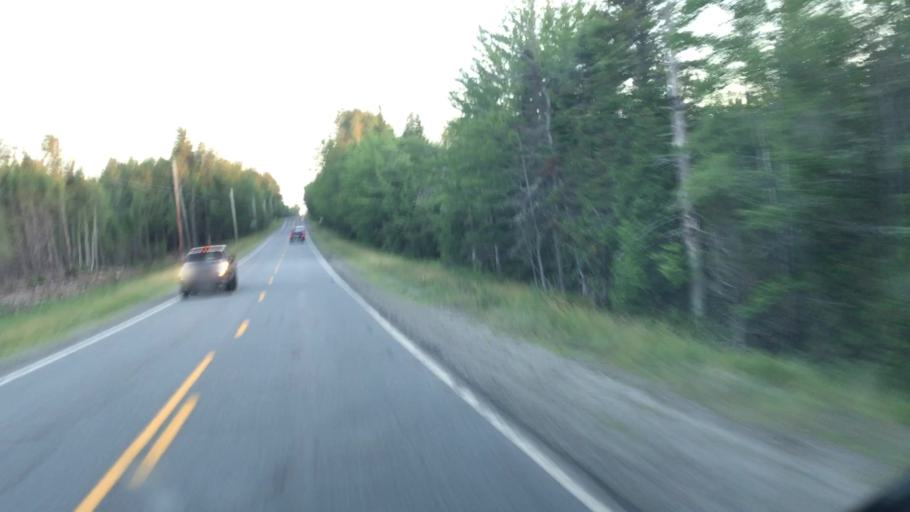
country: US
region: Maine
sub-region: Penobscot County
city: Medway
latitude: 45.5898
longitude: -68.3134
